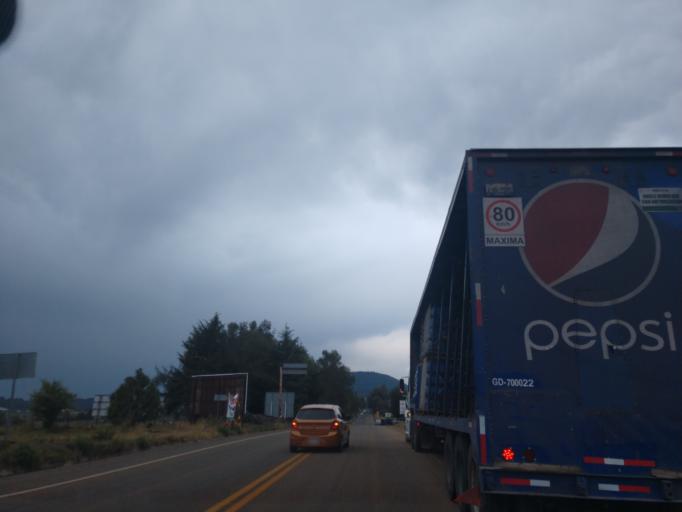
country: MX
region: Jalisco
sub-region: Mazamitla
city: Mazamitla
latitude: 19.9331
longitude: -103.0409
